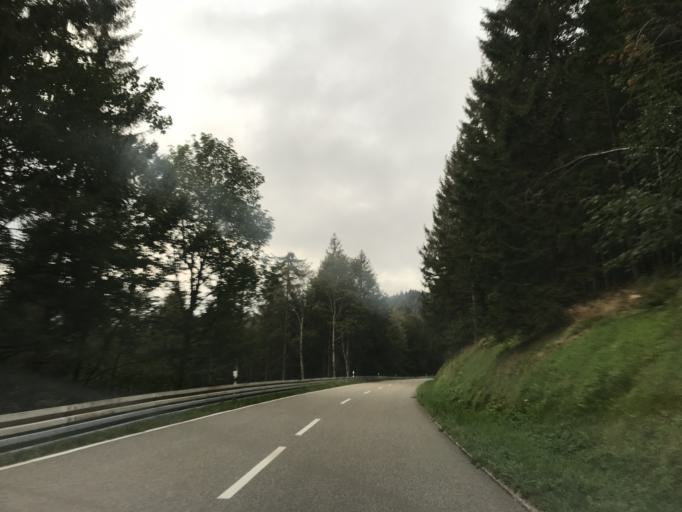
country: DE
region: Baden-Wuerttemberg
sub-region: Freiburg Region
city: Horben
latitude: 47.9127
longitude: 7.8840
